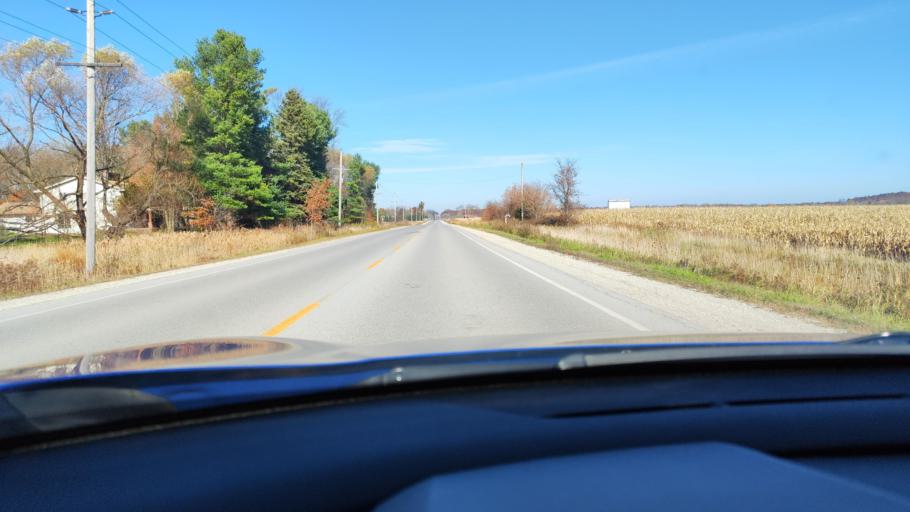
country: CA
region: Ontario
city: Wasaga Beach
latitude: 44.4493
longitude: -80.0697
